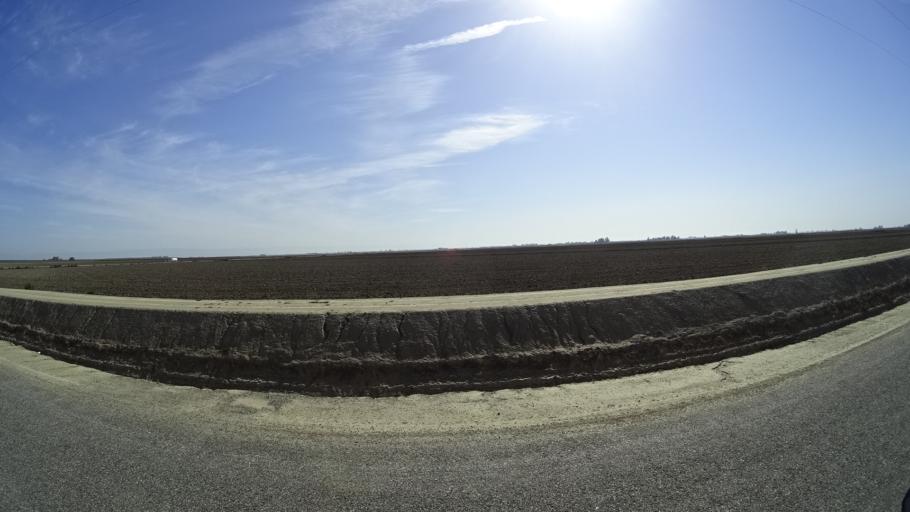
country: US
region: California
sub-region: Glenn County
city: Willows
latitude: 39.6095
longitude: -122.1168
